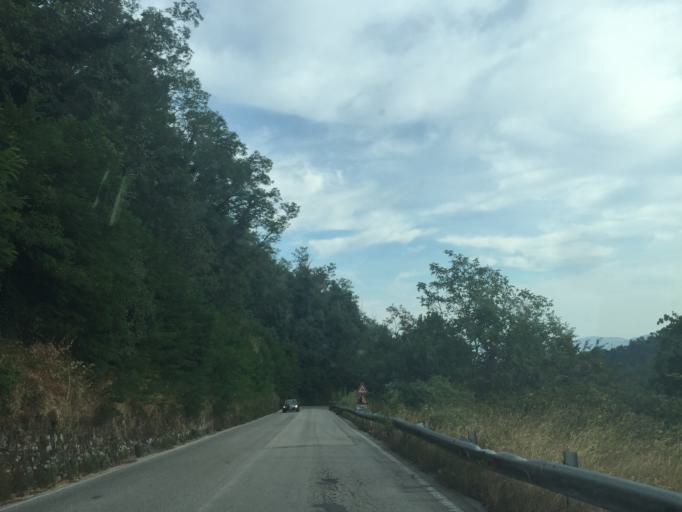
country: IT
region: Tuscany
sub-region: Provincia di Pistoia
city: Campo Tizzoro
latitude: 43.9827
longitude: 10.8625
